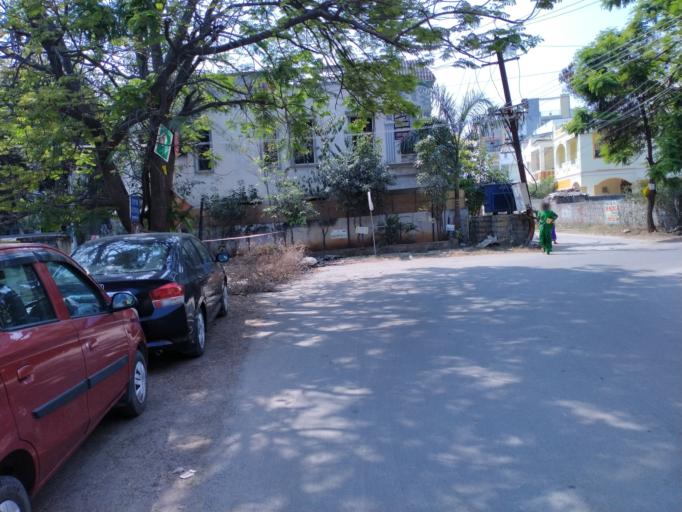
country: IN
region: Telangana
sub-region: Rangareddi
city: Secunderabad
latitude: 17.4971
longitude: 78.5461
